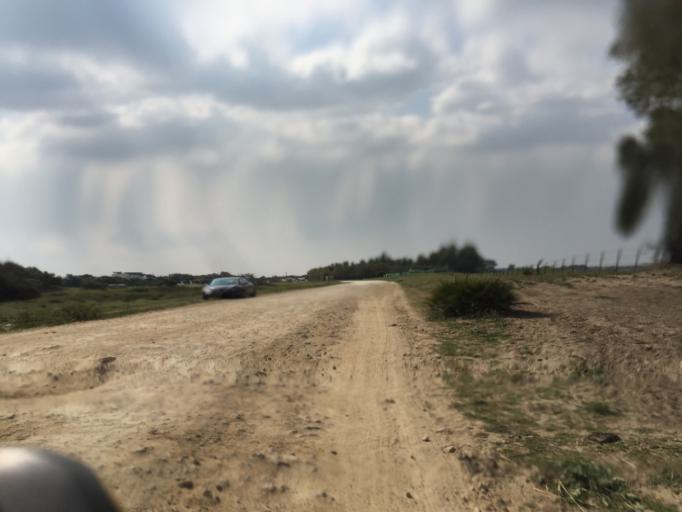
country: ES
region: Andalusia
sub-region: Provincia de Cadiz
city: Benalup-Casas Viejas
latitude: 36.3253
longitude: -5.8841
